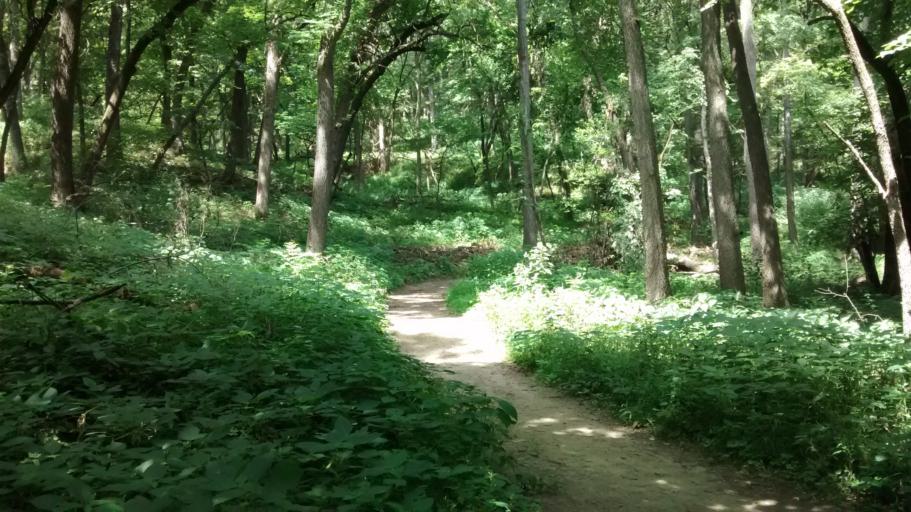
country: US
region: South Dakota
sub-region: Union County
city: North Sioux City
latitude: 42.5465
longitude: -96.4647
